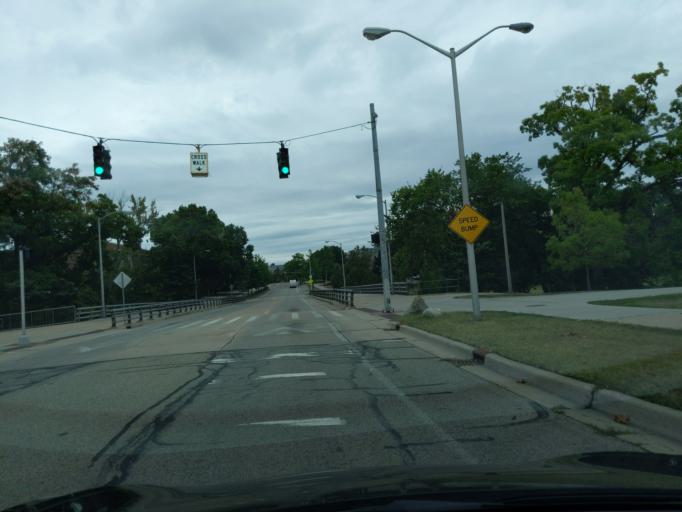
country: US
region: Michigan
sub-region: Ingham County
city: East Lansing
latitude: 42.7270
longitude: -84.4779
